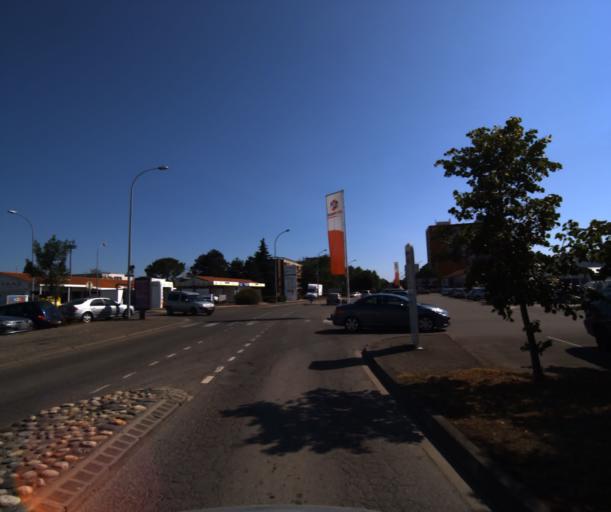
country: FR
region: Midi-Pyrenees
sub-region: Departement de la Haute-Garonne
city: Muret
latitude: 43.4727
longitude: 1.3327
